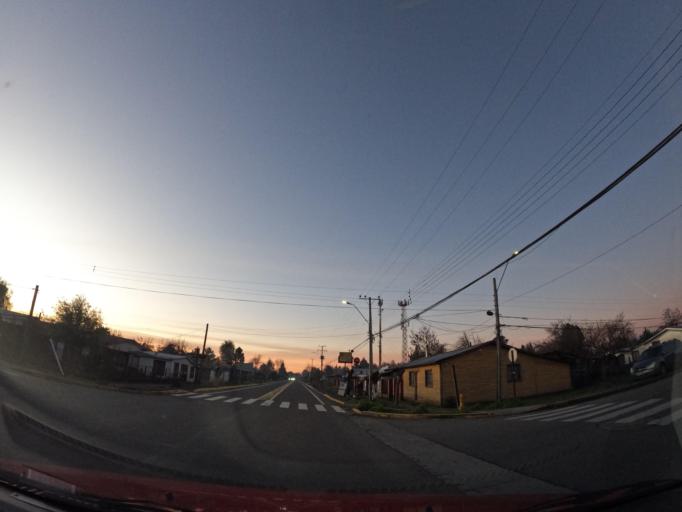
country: CL
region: Biobio
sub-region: Provincia de Biobio
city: Los Angeles
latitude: -37.2889
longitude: -71.9498
